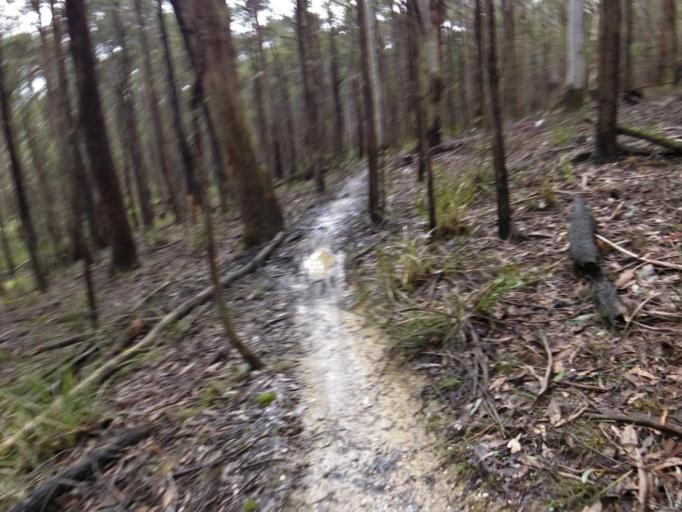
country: AU
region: Victoria
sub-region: Moorabool
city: Bacchus Marsh
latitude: -37.4246
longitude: 144.4804
